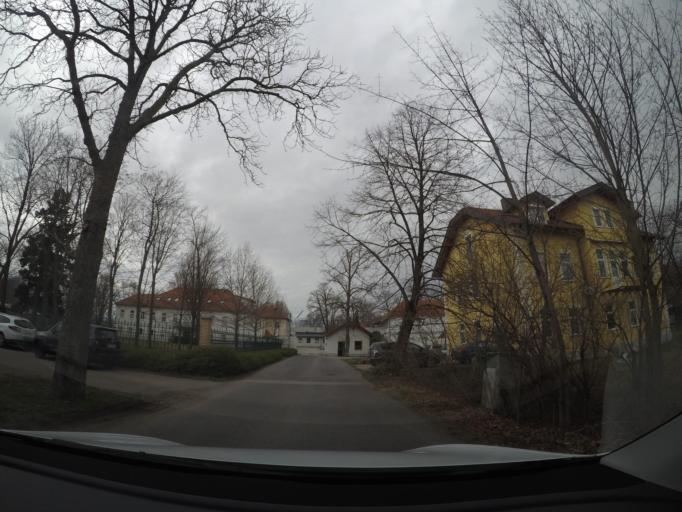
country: AT
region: Lower Austria
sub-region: Politischer Bezirk Baden
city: Ebreichsdorf
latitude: 47.9433
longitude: 16.3953
